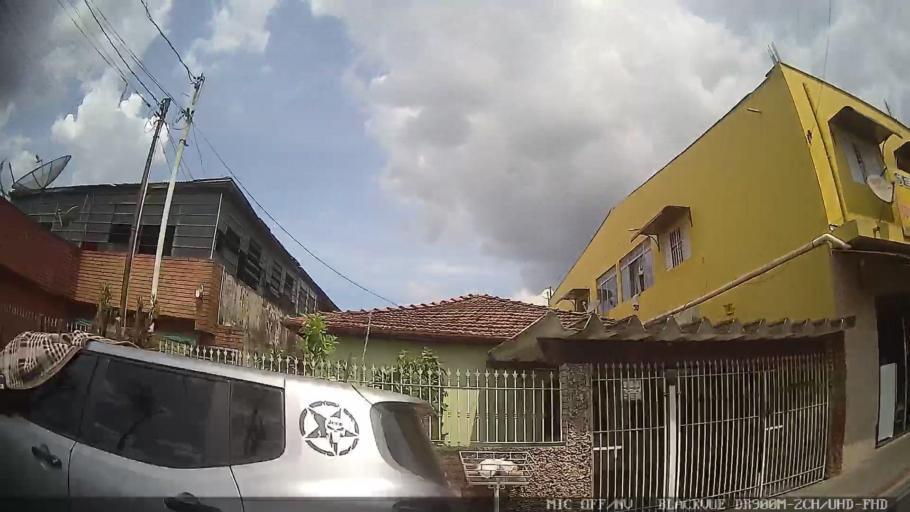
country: BR
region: Sao Paulo
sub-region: Poa
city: Poa
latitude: -23.5275
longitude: -46.3370
